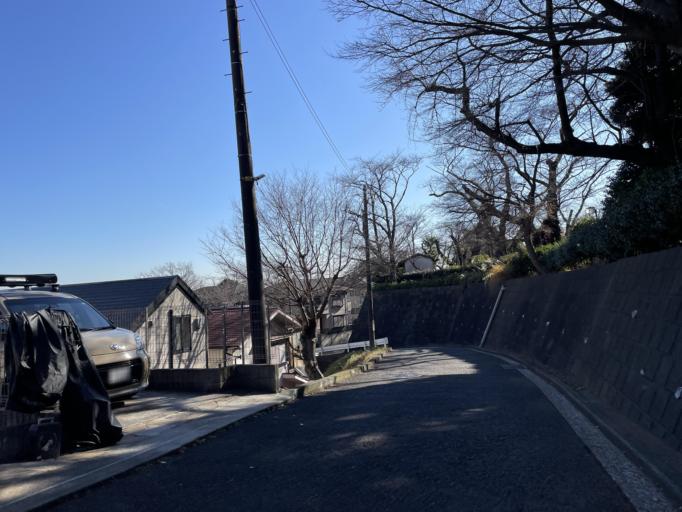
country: JP
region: Kanagawa
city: Yokohama
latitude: 35.4835
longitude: 139.6324
